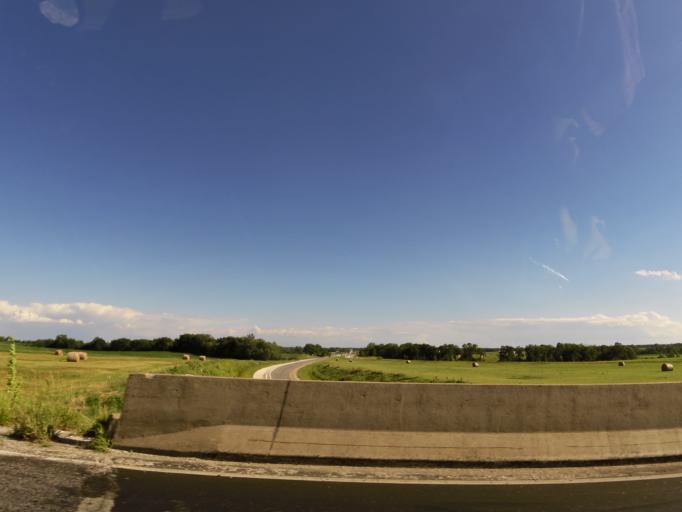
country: US
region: Missouri
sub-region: Marion County
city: Palmyra
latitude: 39.7440
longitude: -91.5102
